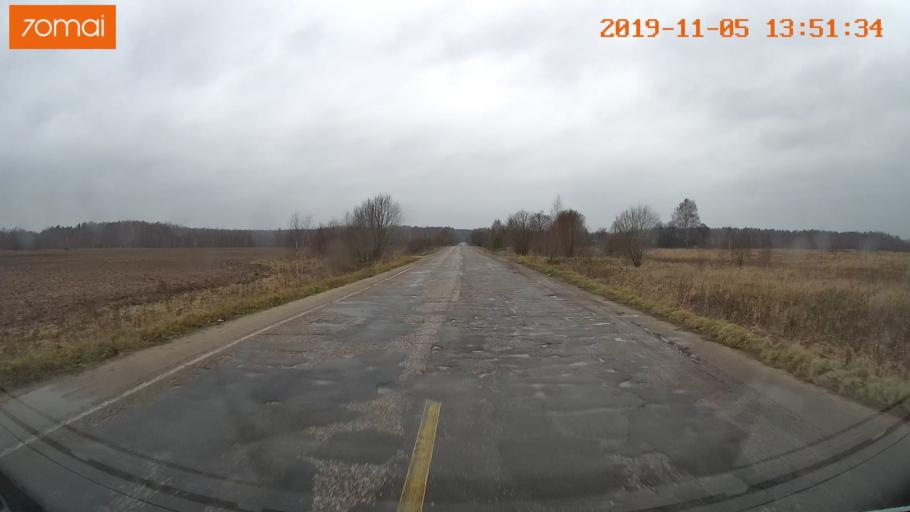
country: RU
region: Ivanovo
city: Kaminskiy
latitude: 57.0251
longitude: 41.3992
